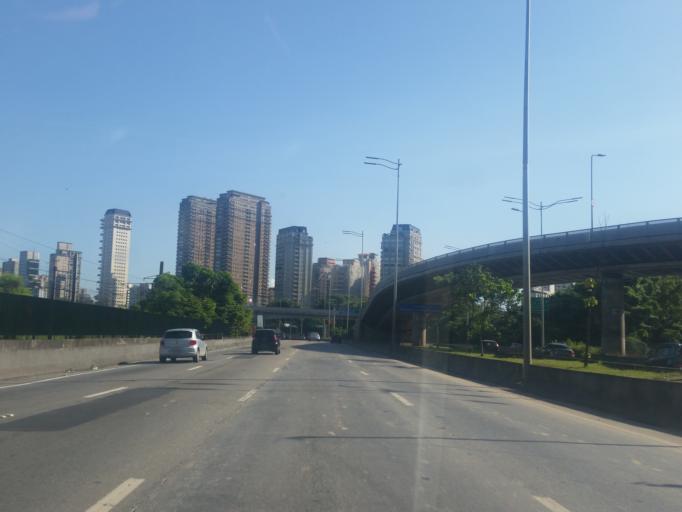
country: BR
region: Sao Paulo
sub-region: Sao Paulo
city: Sao Paulo
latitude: -23.5899
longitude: -46.6913
